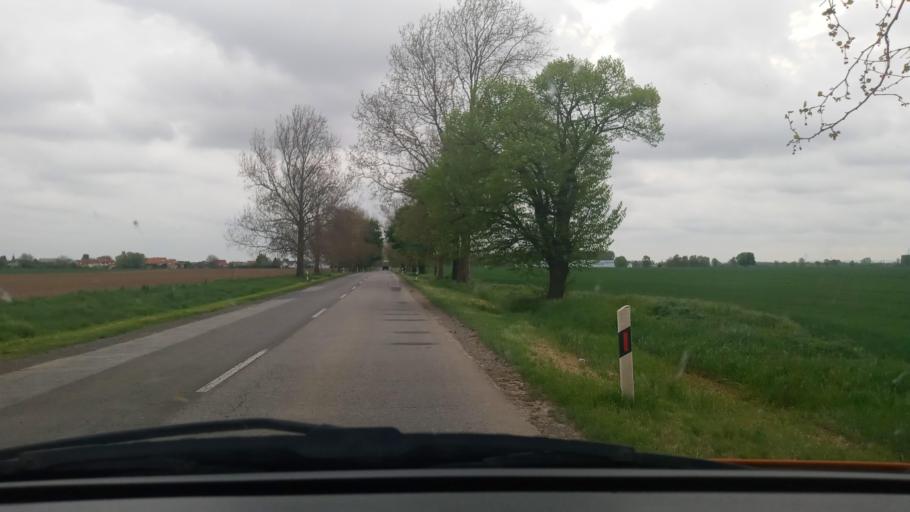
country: HU
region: Baranya
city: Boly
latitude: 45.9874
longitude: 18.5217
